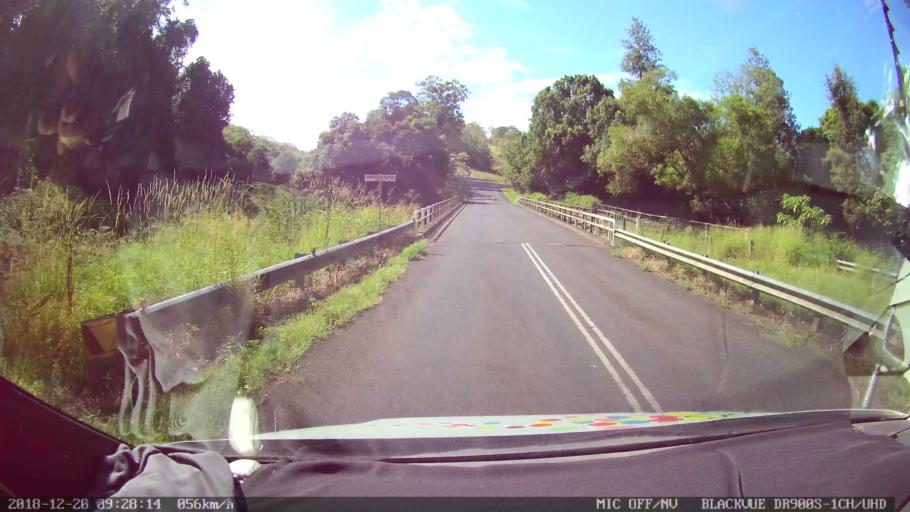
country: AU
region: New South Wales
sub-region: Lismore Municipality
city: Nimbin
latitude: -28.6800
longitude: 153.2837
